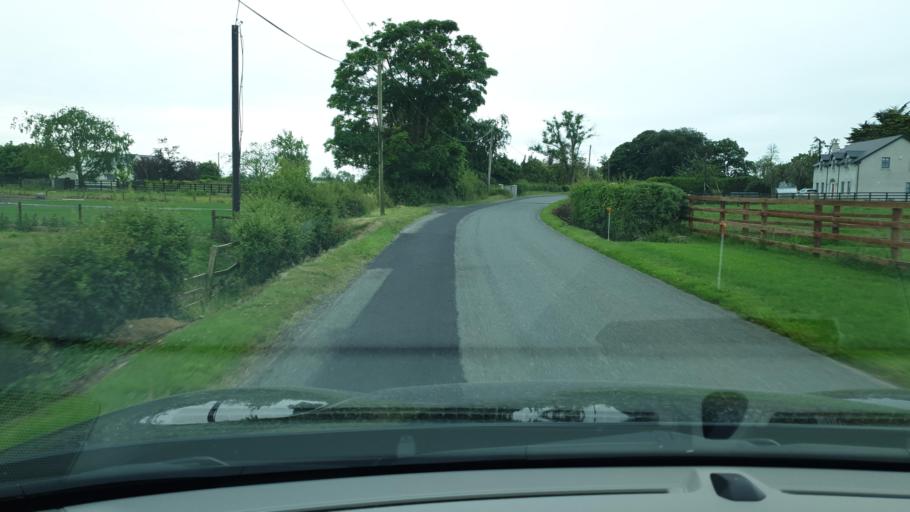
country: IE
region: Leinster
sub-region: An Mhi
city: Ashbourne
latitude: 53.4639
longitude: -6.3801
